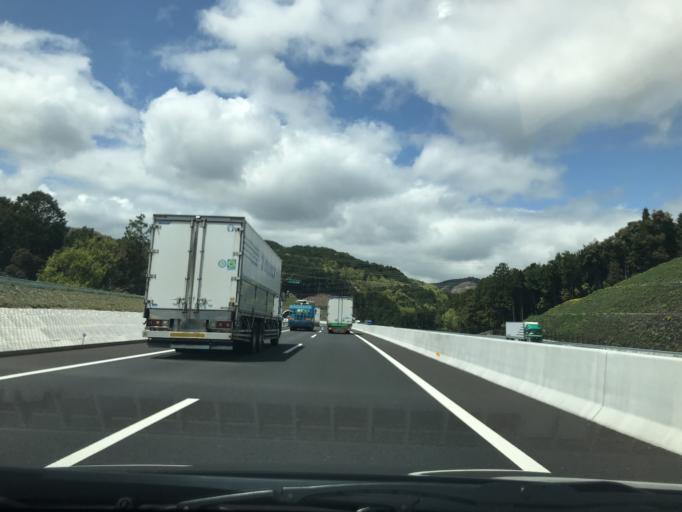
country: JP
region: Osaka
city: Takatsuki
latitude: 34.8990
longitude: 135.6045
